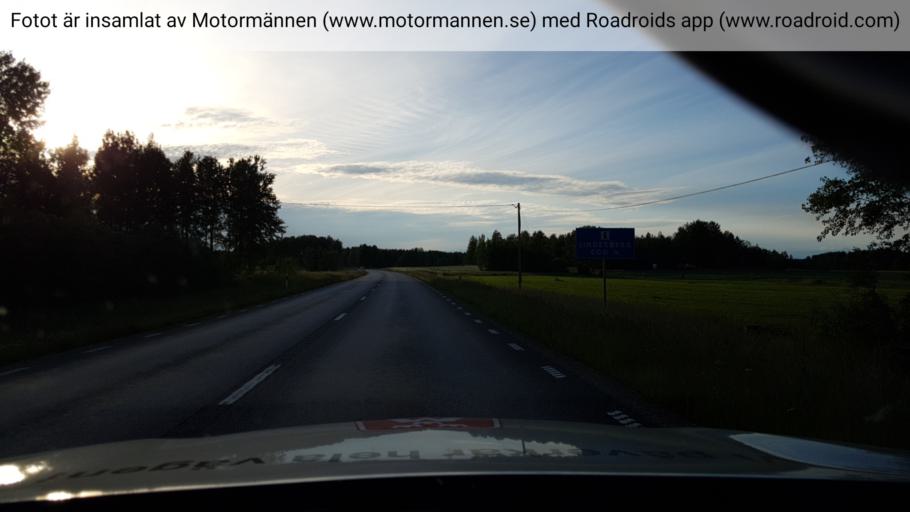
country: SE
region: OErebro
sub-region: Lindesbergs Kommun
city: Lindesberg
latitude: 59.5442
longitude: 15.2460
